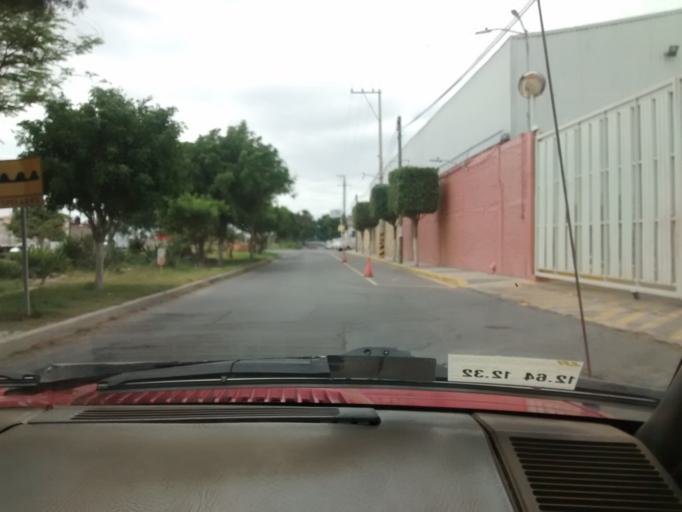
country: MX
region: Puebla
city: Tehuacan
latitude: 18.4790
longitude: -97.4110
